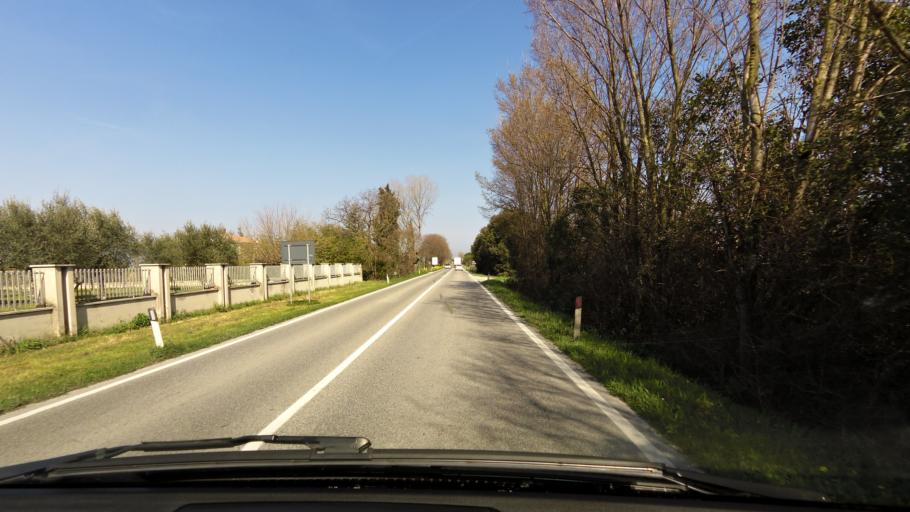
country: IT
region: The Marches
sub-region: Provincia di Macerata
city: Potenza Picena
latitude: 43.3960
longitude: 13.6470
